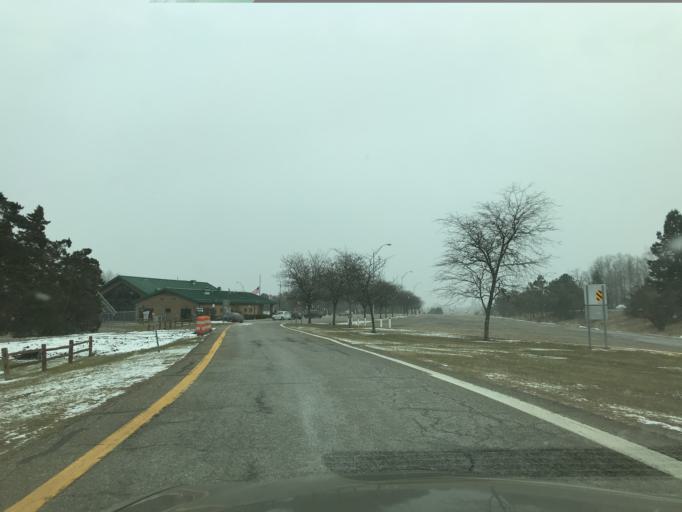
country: US
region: Michigan
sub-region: Clare County
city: Clare
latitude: 43.8512
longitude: -84.7781
